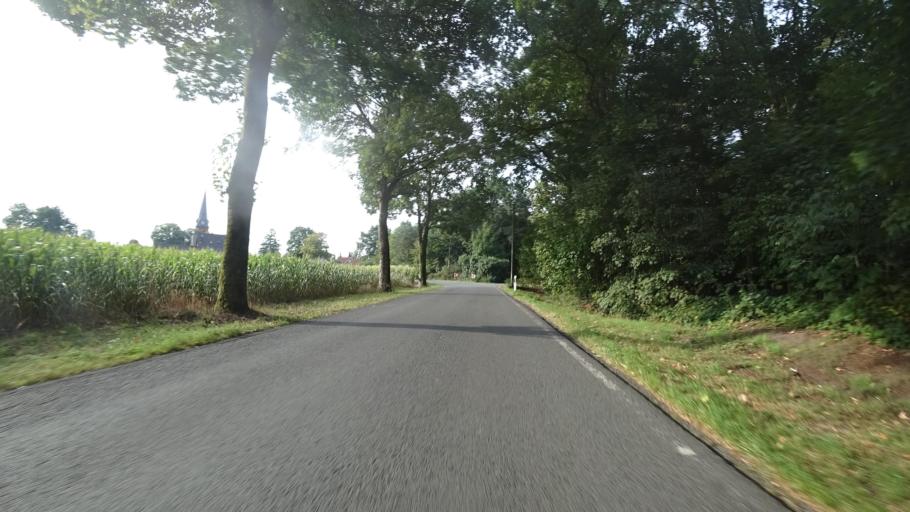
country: DE
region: North Rhine-Westphalia
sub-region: Regierungsbezirk Detmold
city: Steinhagen
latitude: 51.9753
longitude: 8.4625
